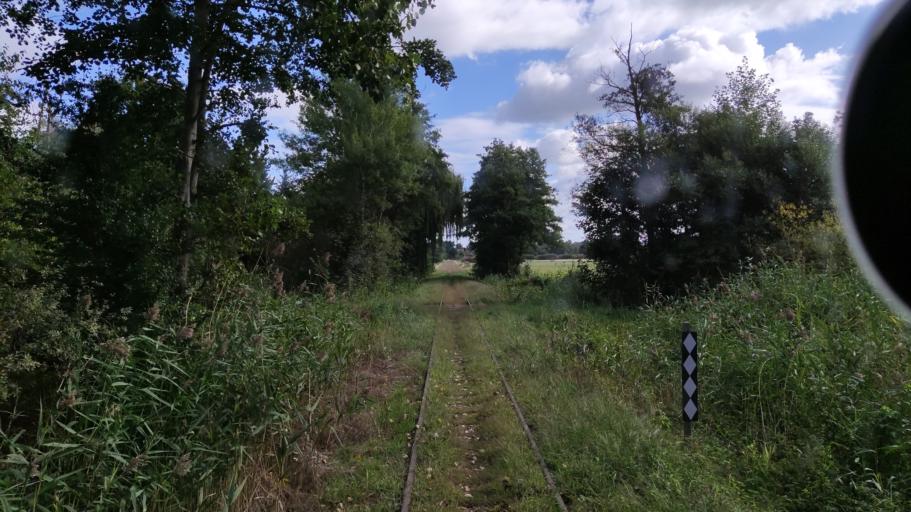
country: DE
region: Lower Saxony
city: Bleckede
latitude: 53.2933
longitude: 10.7130
